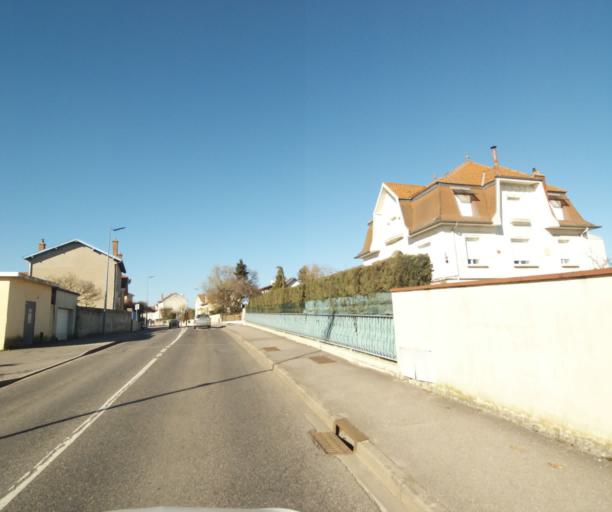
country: FR
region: Lorraine
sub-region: Departement de Meurthe-et-Moselle
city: Tomblaine
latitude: 48.6827
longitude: 6.2157
